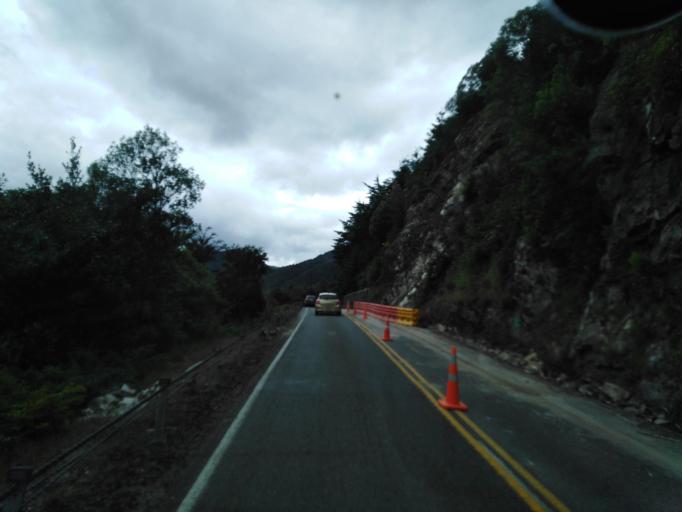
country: NZ
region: Tasman
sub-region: Tasman District
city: Wakefield
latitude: -41.7096
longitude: 172.5445
